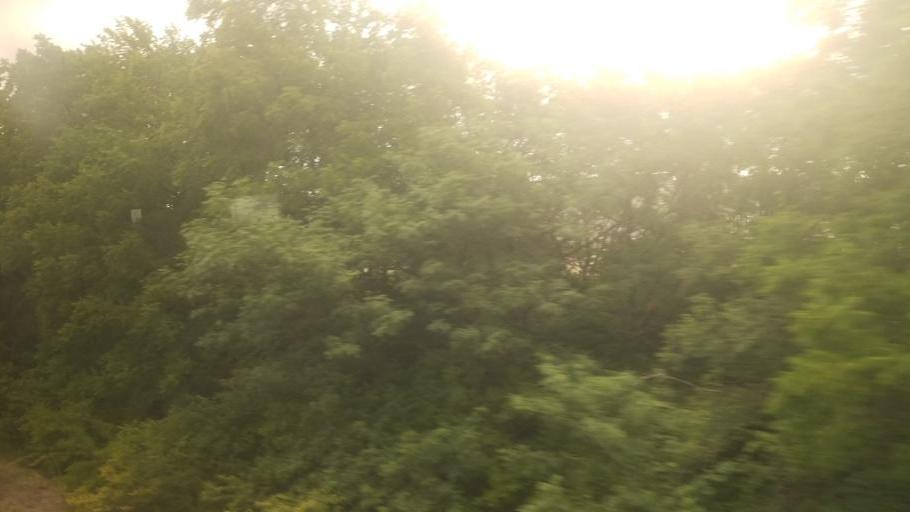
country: US
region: Kansas
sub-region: Shawnee County
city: Topeka
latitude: 39.0165
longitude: -95.6780
